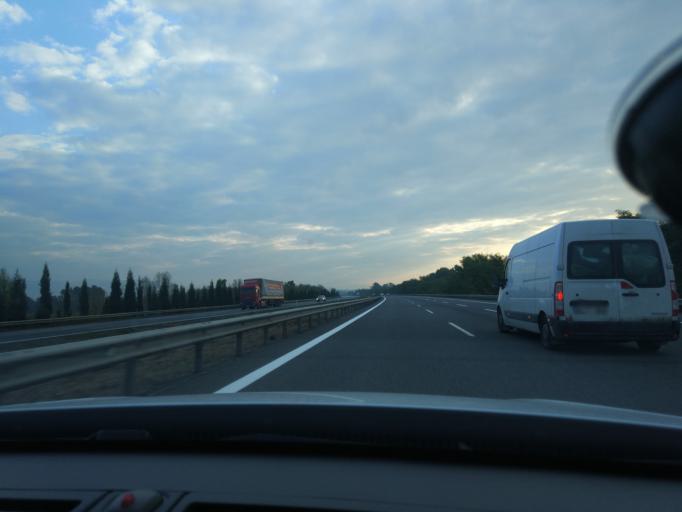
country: TR
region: Sakarya
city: Akyazi
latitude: 40.7440
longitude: 30.6701
